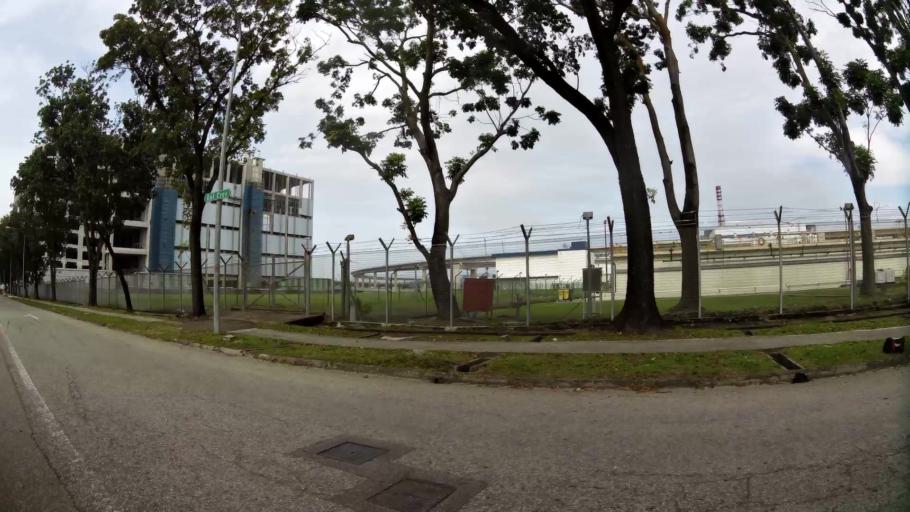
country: MY
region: Johor
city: Johor Bahru
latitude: 1.3157
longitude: 103.6602
